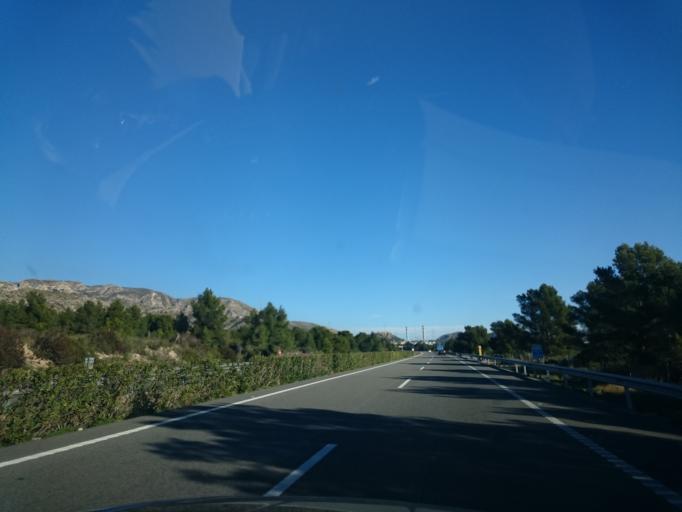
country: ES
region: Catalonia
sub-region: Provincia de Tarragona
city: l'Ametlla de Mar
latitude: 40.9443
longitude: 0.8556
